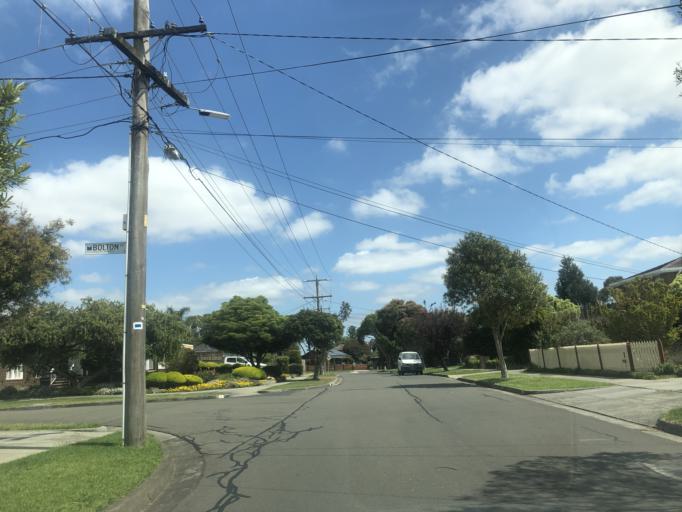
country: AU
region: Victoria
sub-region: Monash
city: Mulgrave
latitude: -37.9209
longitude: 145.1707
